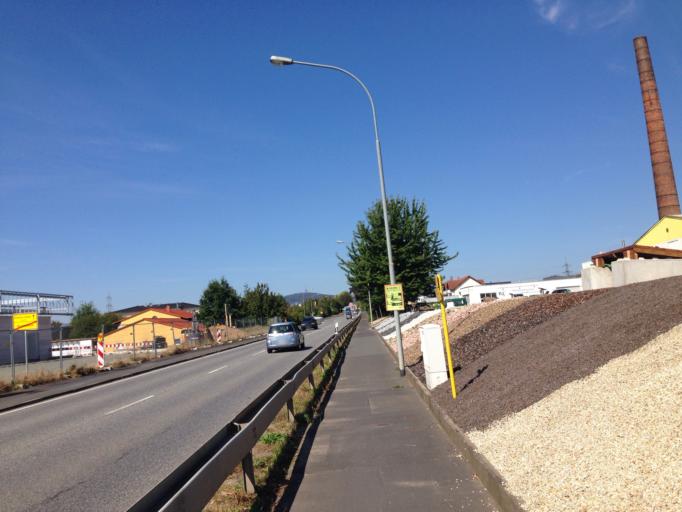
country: DE
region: Hesse
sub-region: Regierungsbezirk Giessen
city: Heuchelheim
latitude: 50.5992
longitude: 8.6270
